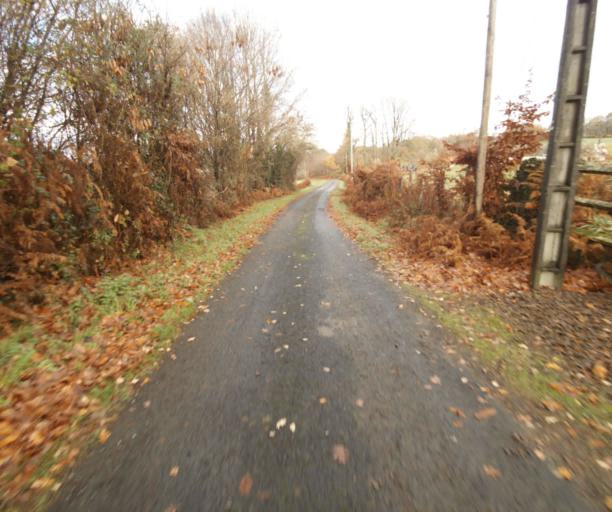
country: FR
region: Limousin
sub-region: Departement de la Correze
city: Saint-Mexant
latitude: 45.2491
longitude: 1.6480
